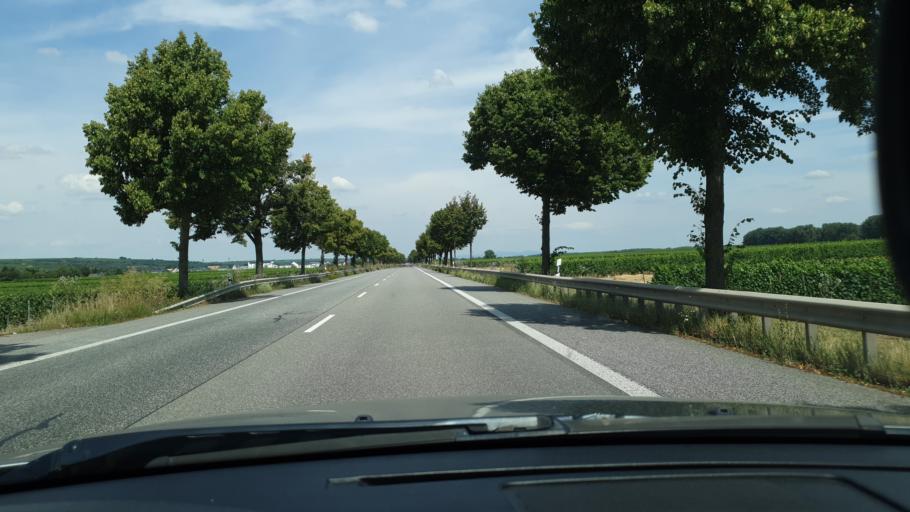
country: DE
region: Rheinland-Pfalz
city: Alsheim
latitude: 49.7577
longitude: 8.3523
